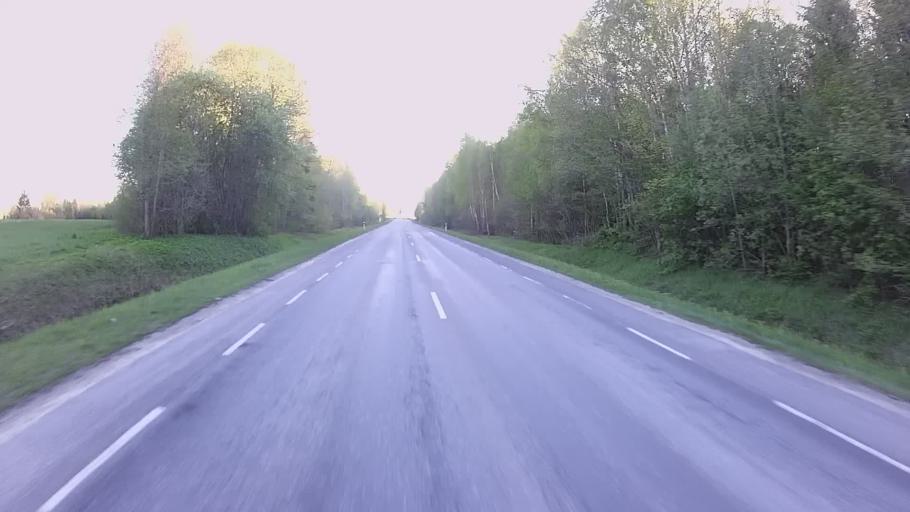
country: EE
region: Viljandimaa
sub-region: Viiratsi vald
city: Viiratsi
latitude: 58.4182
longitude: 25.6958
